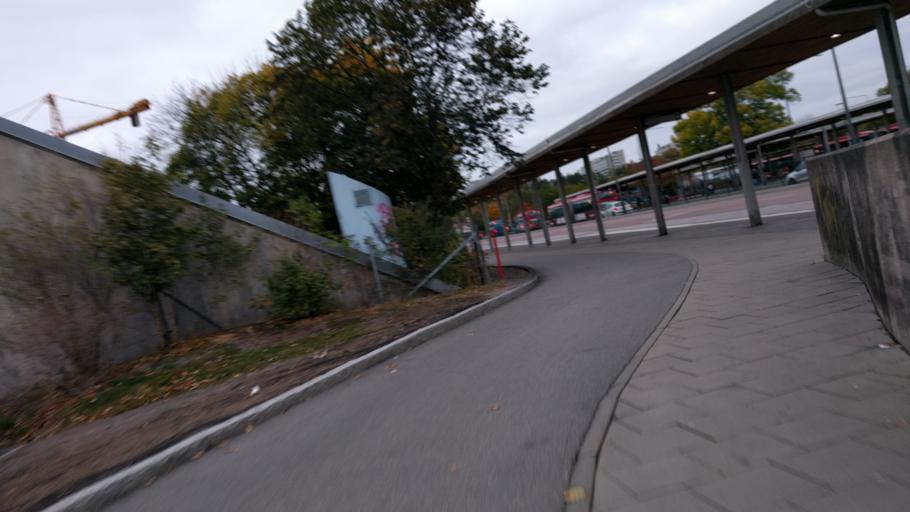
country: SE
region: Stockholm
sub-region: Norrtalje Kommun
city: Bergshamra
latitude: 59.3900
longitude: 18.0419
